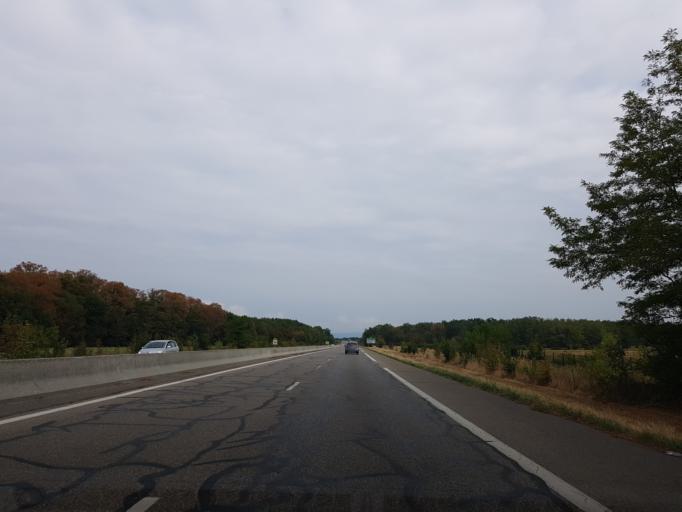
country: FR
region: Alsace
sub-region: Departement du Haut-Rhin
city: Pulversheim
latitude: 47.8055
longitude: 7.3031
